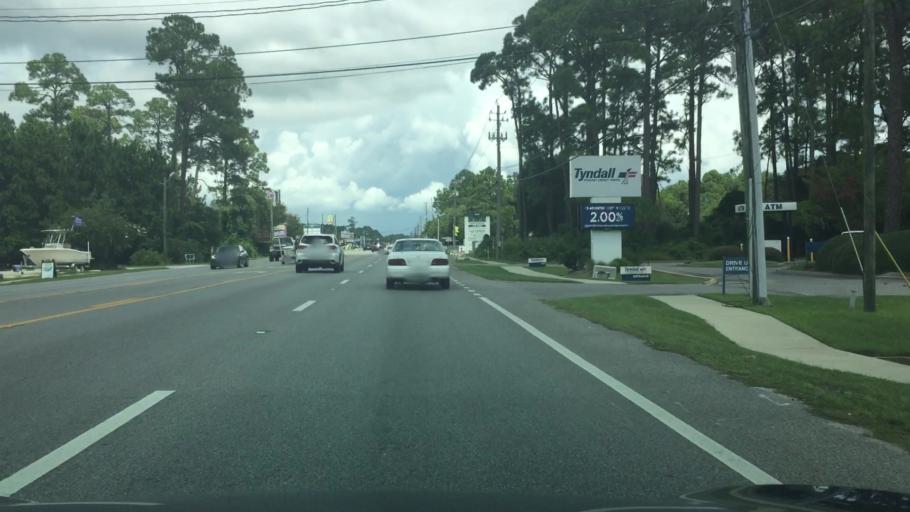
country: US
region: Florida
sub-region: Bay County
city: Upper Grand Lagoon
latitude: 30.1628
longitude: -85.7550
